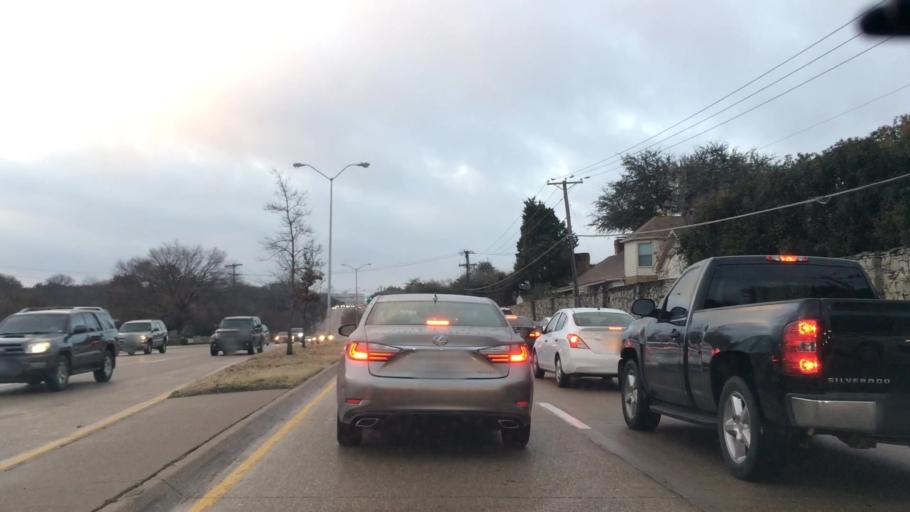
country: US
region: Texas
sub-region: Dallas County
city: Addison
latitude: 32.9671
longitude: -96.8045
